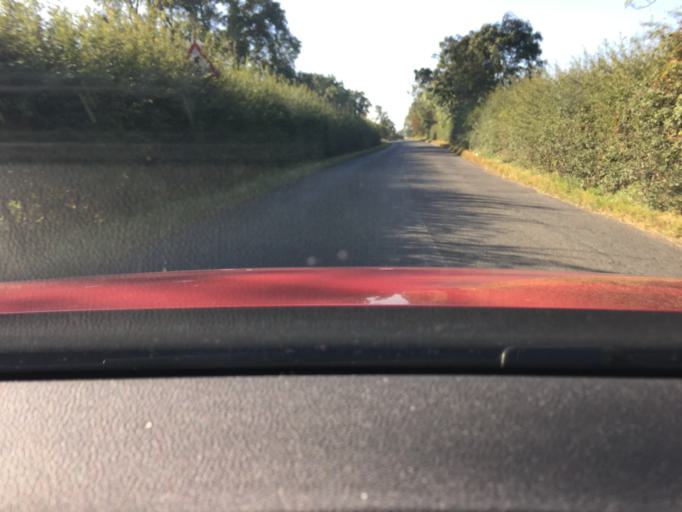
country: GB
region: England
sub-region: Leicestershire
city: Houghton on the Hill
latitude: 52.6629
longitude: -1.0233
